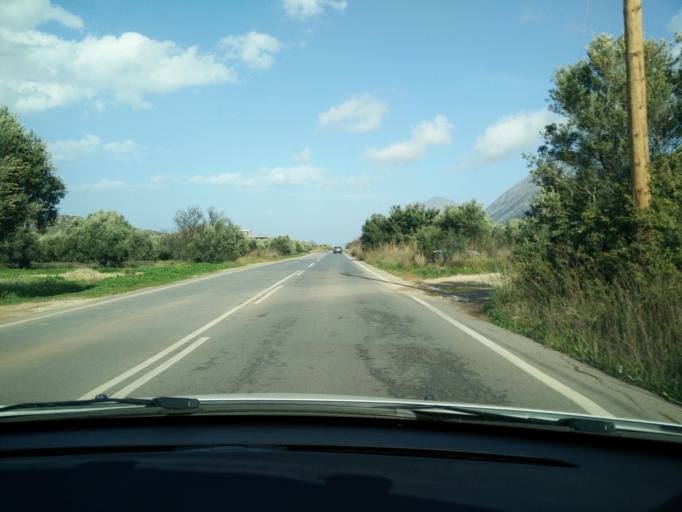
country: GR
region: Crete
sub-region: Nomos Lasithiou
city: Kato Chorio
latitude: 35.0670
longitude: 25.8007
